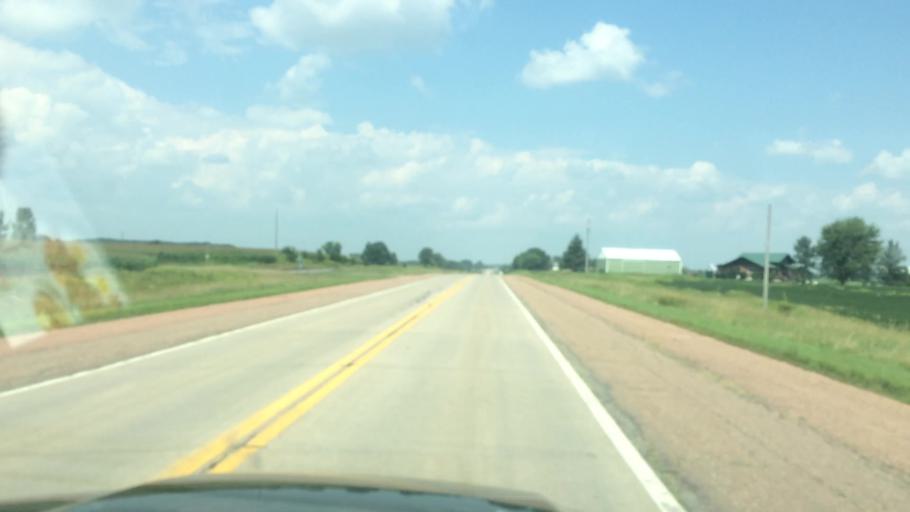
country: US
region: Wisconsin
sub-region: Clark County
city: Colby
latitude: 44.8634
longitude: -90.3158
